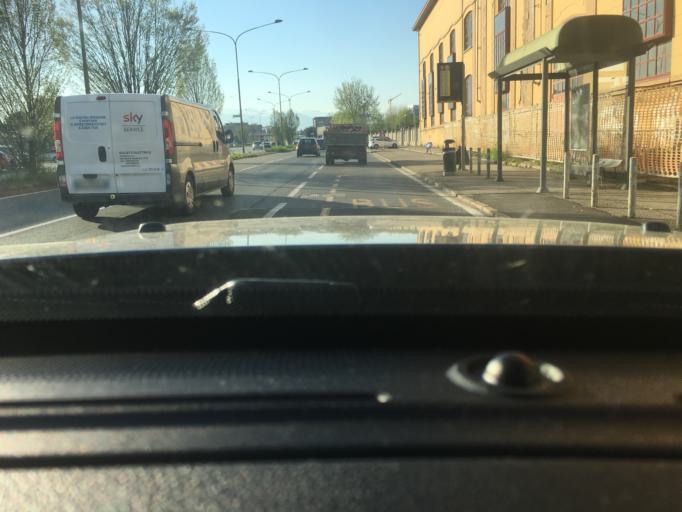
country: IT
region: Piedmont
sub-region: Provincia di Torino
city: Turin
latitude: 45.0997
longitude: 7.7087
